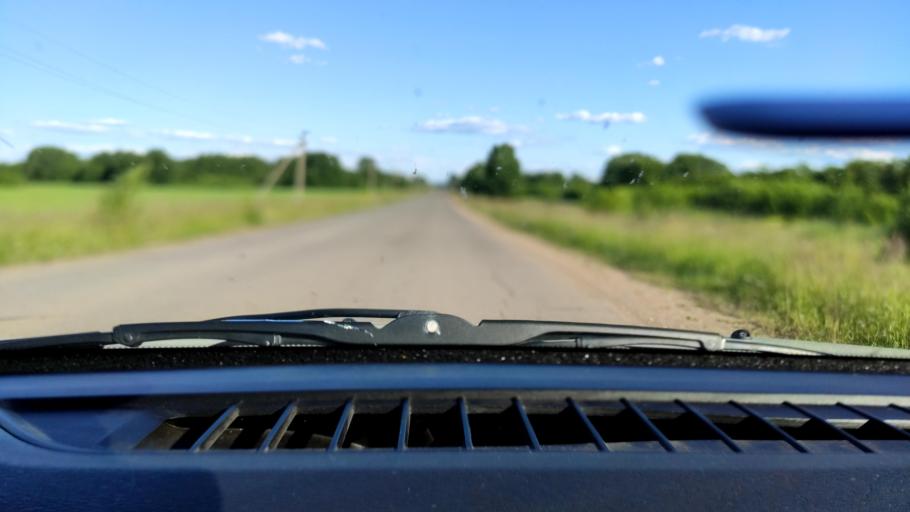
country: RU
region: Perm
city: Uinskoye
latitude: 57.0994
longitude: 56.5431
